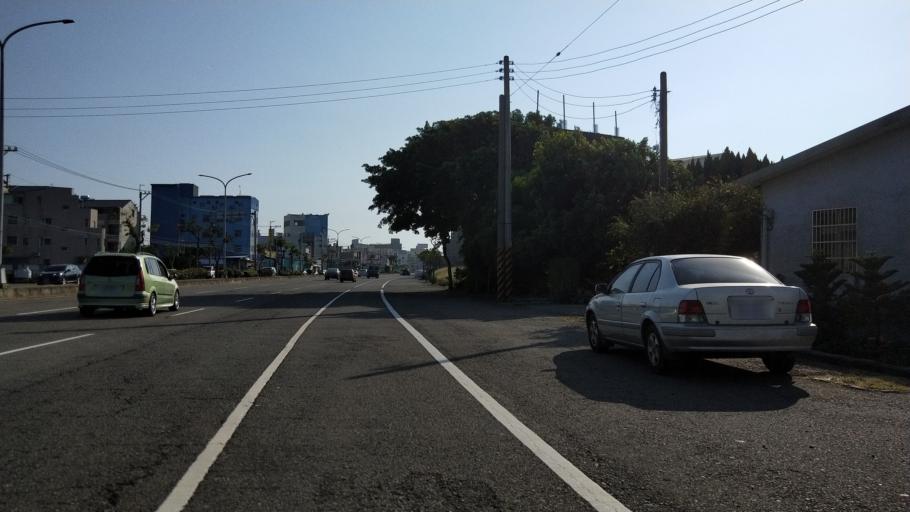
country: TW
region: Taiwan
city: Fengyuan
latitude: 24.2682
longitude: 120.5664
